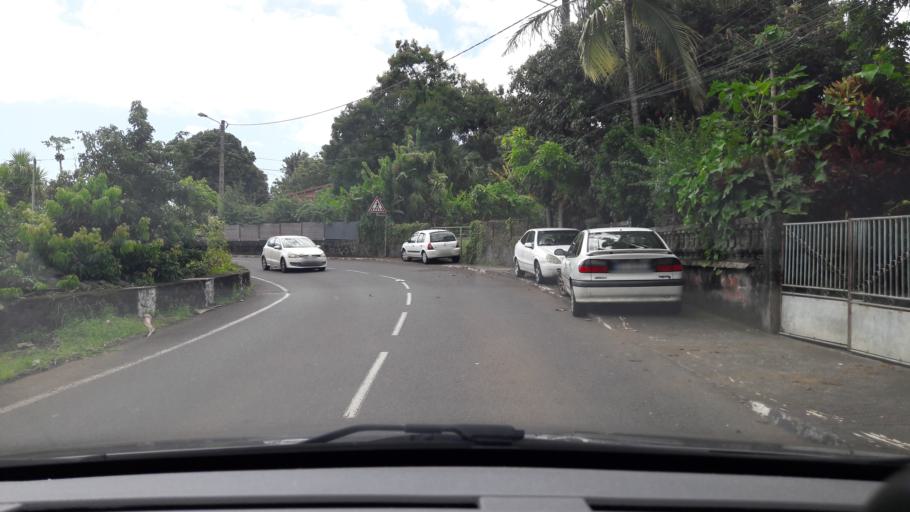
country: RE
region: Reunion
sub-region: Reunion
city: Saint-Benoit
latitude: -21.0809
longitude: 55.6917
